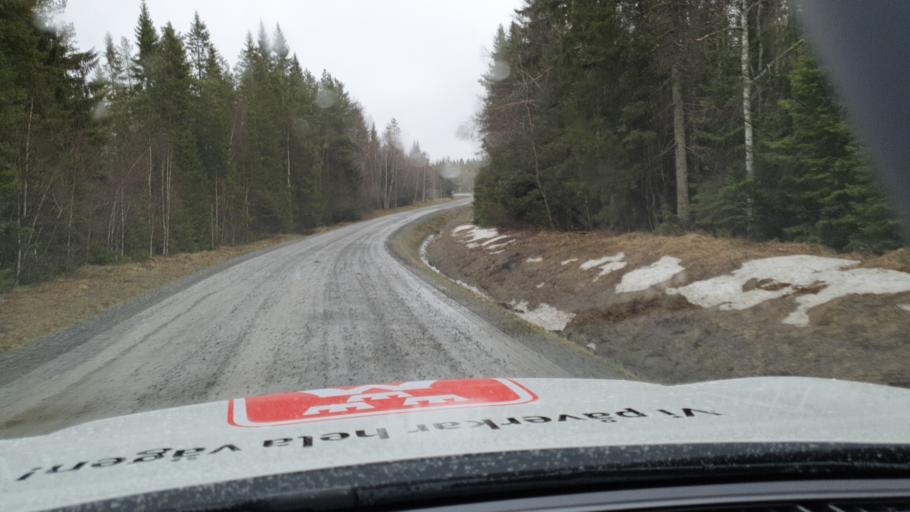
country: SE
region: Jaemtland
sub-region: Krokoms Kommun
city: Valla
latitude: 63.2092
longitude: 14.0193
